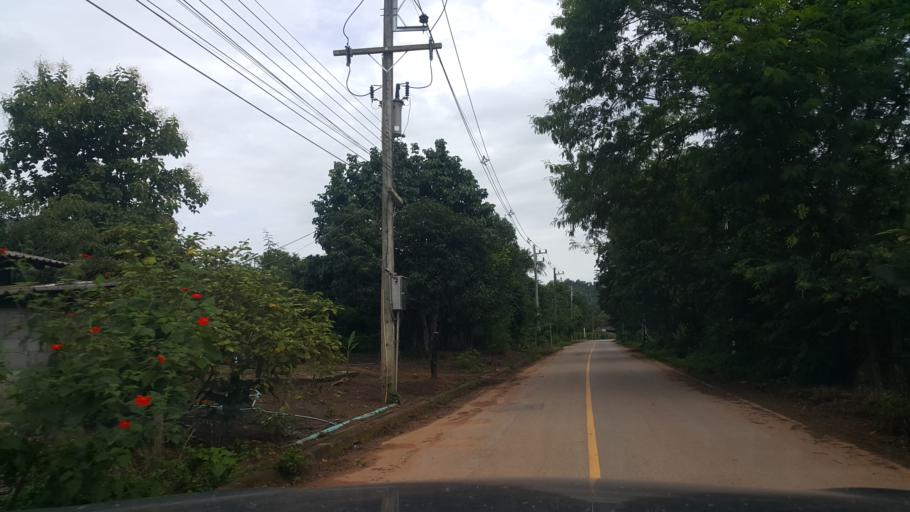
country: TH
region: Chiang Mai
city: San Sai
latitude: 18.9909
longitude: 99.1282
